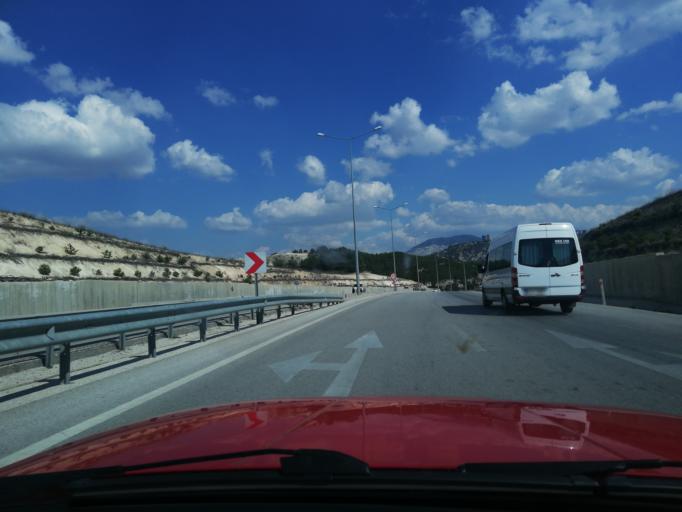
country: TR
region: Burdur
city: Burdur
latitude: 37.7010
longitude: 30.3162
